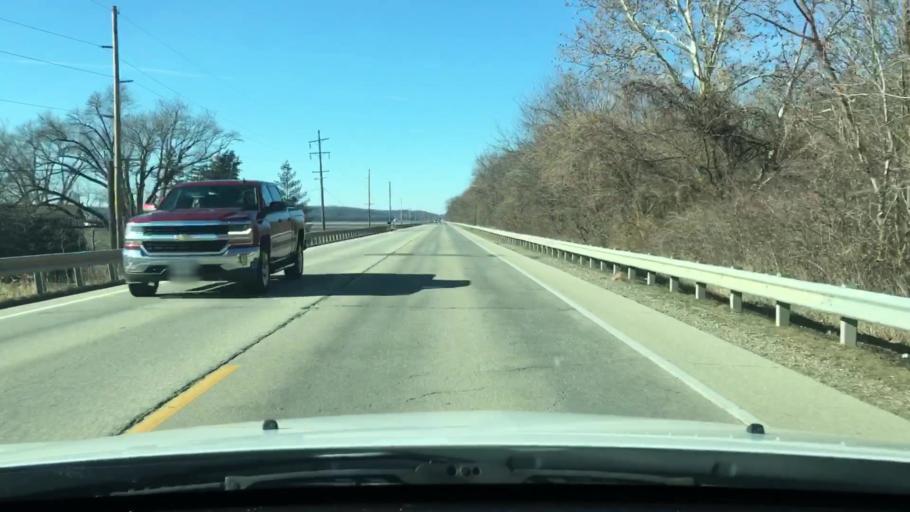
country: US
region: Illinois
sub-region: Mason County
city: Havana
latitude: 40.2982
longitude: -90.0947
